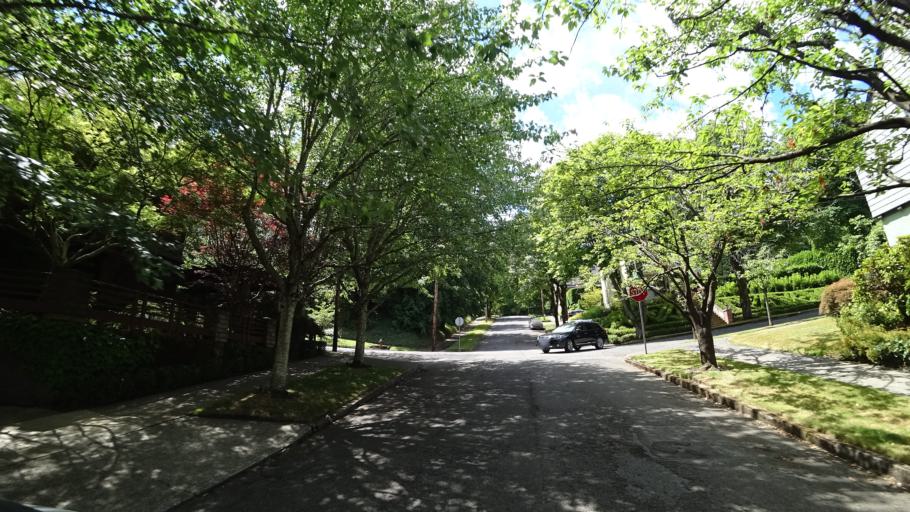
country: US
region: Oregon
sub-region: Multnomah County
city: Portland
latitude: 45.5087
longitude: -122.6963
